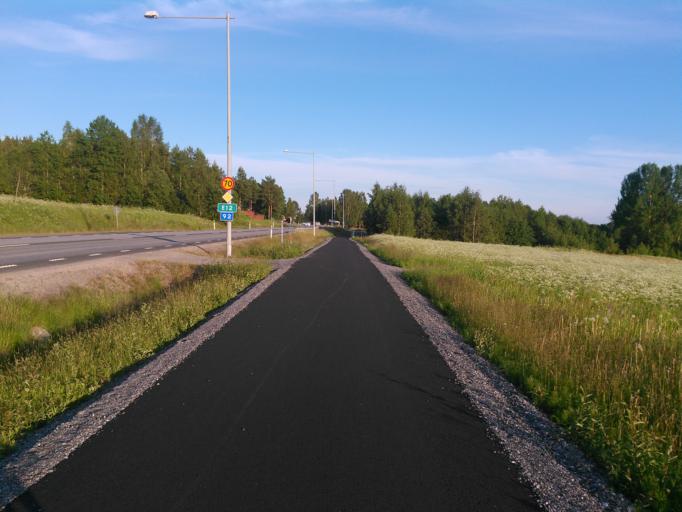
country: SE
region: Vaesterbotten
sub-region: Umea Kommun
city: Roback
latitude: 63.8631
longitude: 20.0868
